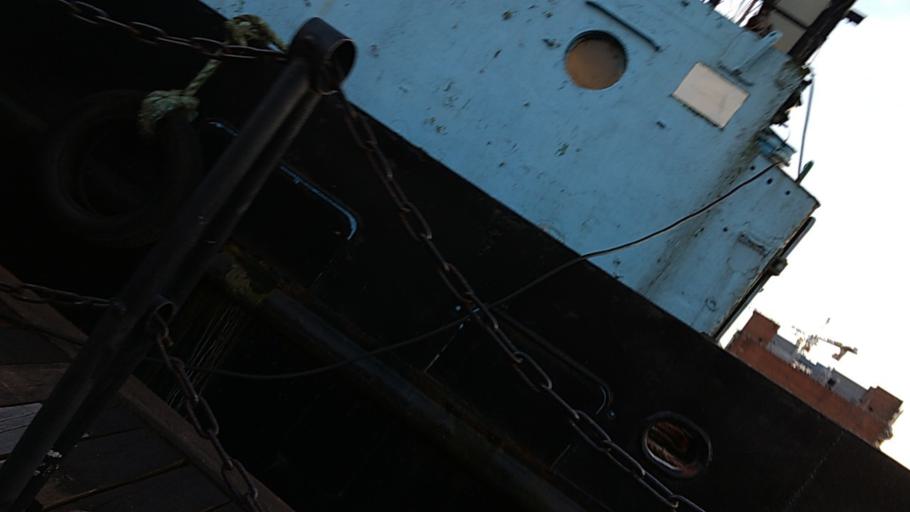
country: PL
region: Pomeranian Voivodeship
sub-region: Gdansk
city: Gdansk
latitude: 54.3506
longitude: 18.6592
